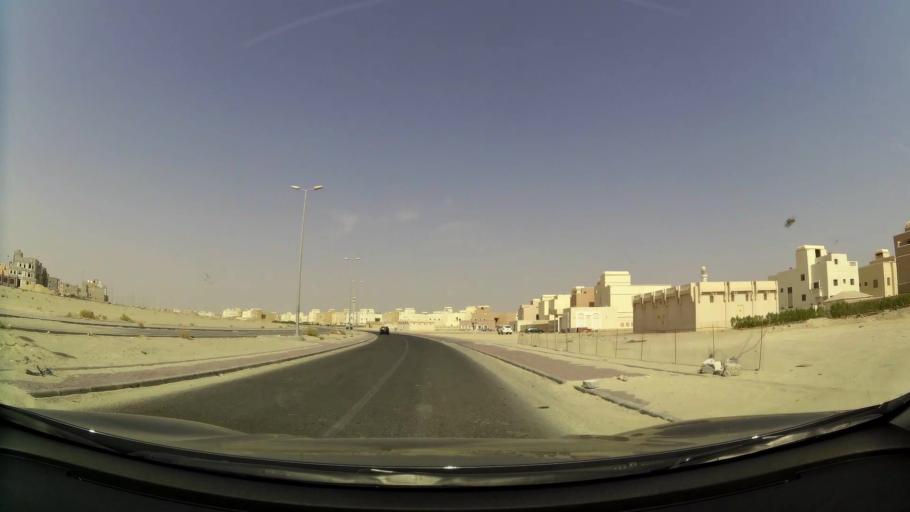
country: KW
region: Al Ahmadi
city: Al Wafrah
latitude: 28.7943
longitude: 48.0656
